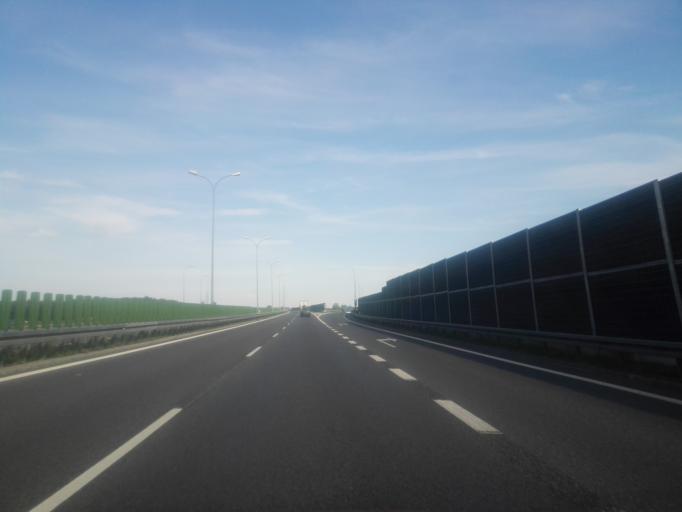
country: PL
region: Lower Silesian Voivodeship
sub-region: Powiat olesnicki
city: Olesnica
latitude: 51.2291
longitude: 17.4326
